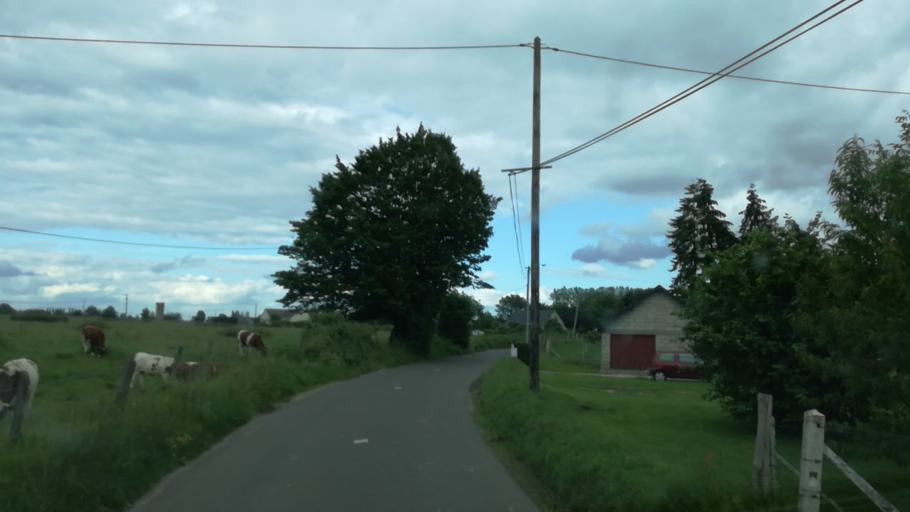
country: FR
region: Haute-Normandie
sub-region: Departement de l'Eure
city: Bourg-Achard
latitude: 49.2996
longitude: 0.8034
